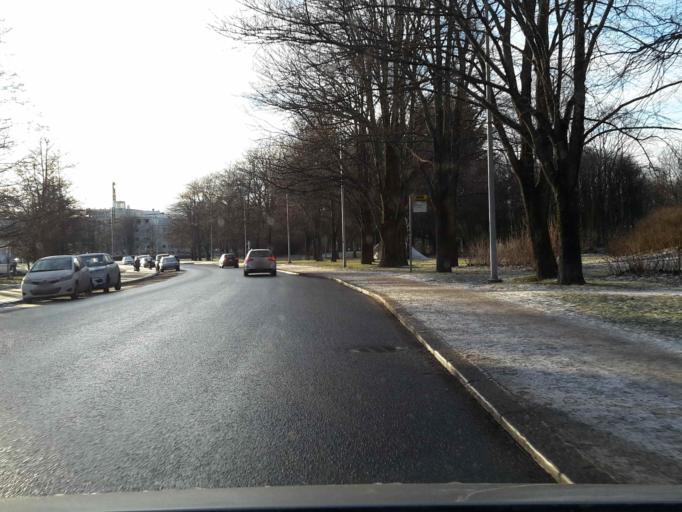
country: FI
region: Uusimaa
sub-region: Helsinki
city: Helsinki
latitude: 60.1591
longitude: 24.8870
